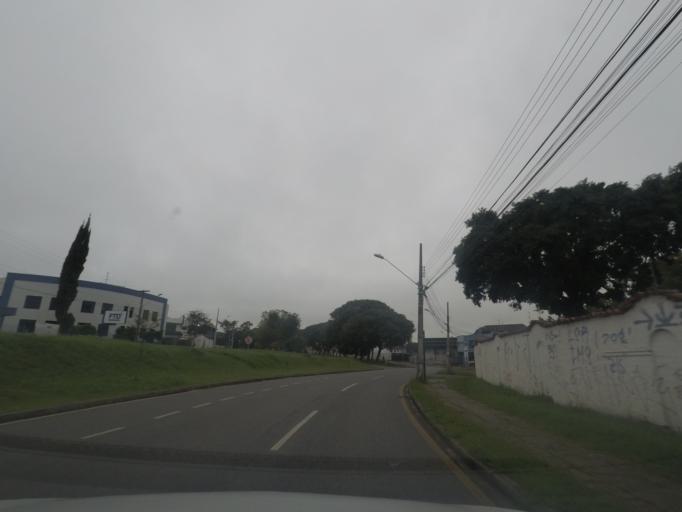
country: BR
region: Parana
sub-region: Curitiba
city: Curitiba
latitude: -25.4528
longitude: -49.2582
